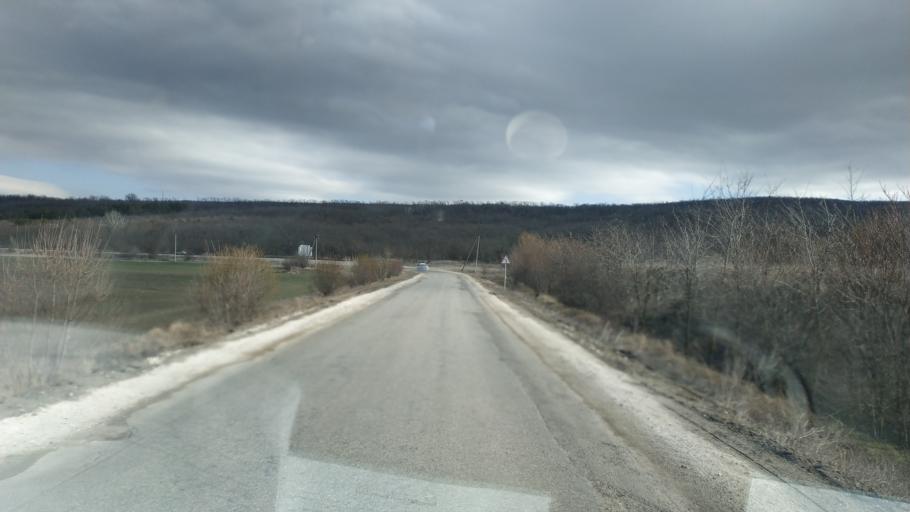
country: MD
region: Causeni
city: Causeni
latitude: 46.6369
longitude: 29.3743
